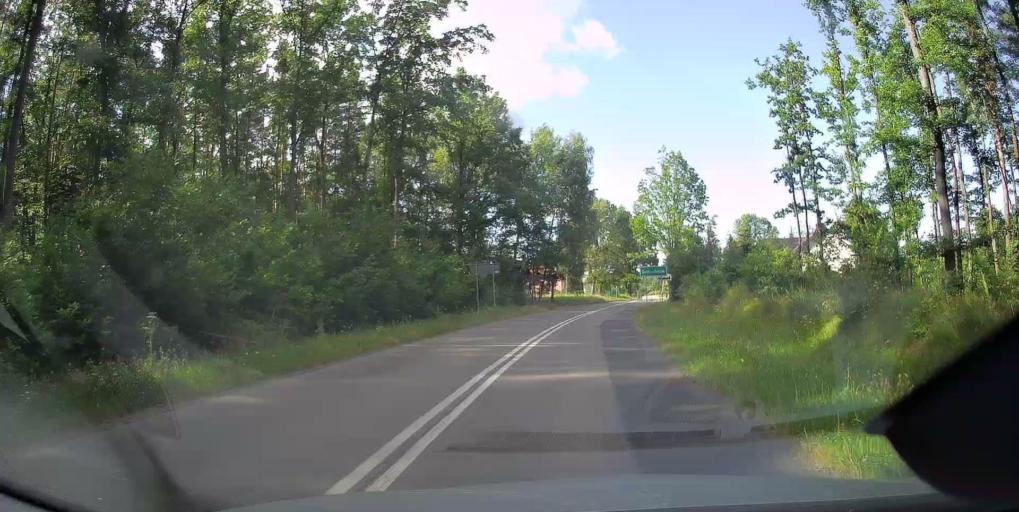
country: PL
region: Swietokrzyskie
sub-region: Powiat skarzyski
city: Suchedniow
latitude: 51.0208
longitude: 20.8379
